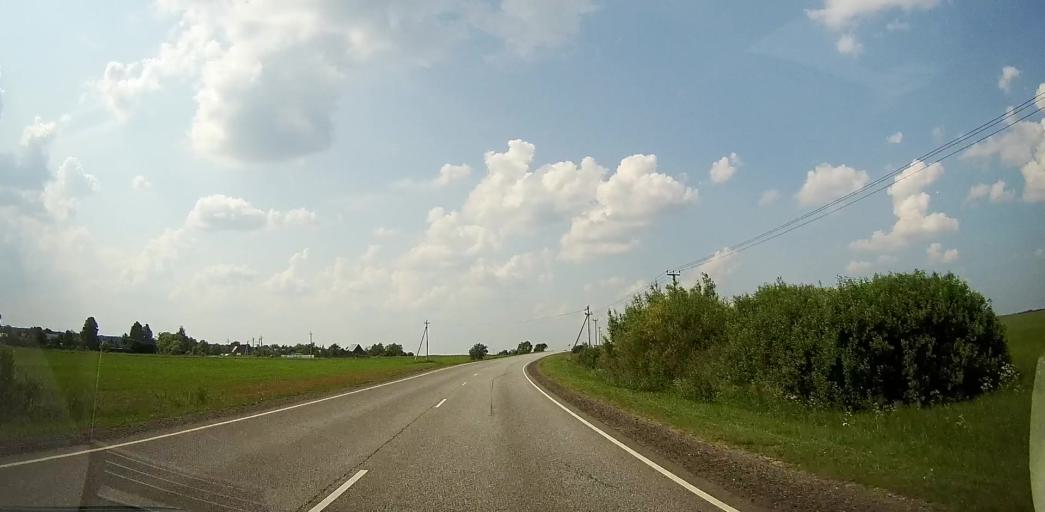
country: RU
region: Moskovskaya
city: Malino
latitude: 55.0320
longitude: 38.1614
